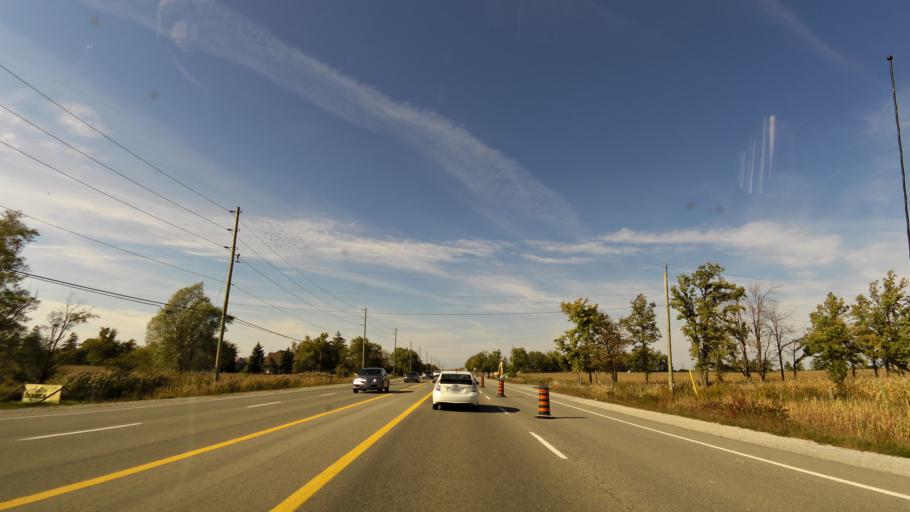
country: CA
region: Ontario
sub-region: Halton
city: Milton
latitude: 43.5495
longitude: -79.8002
